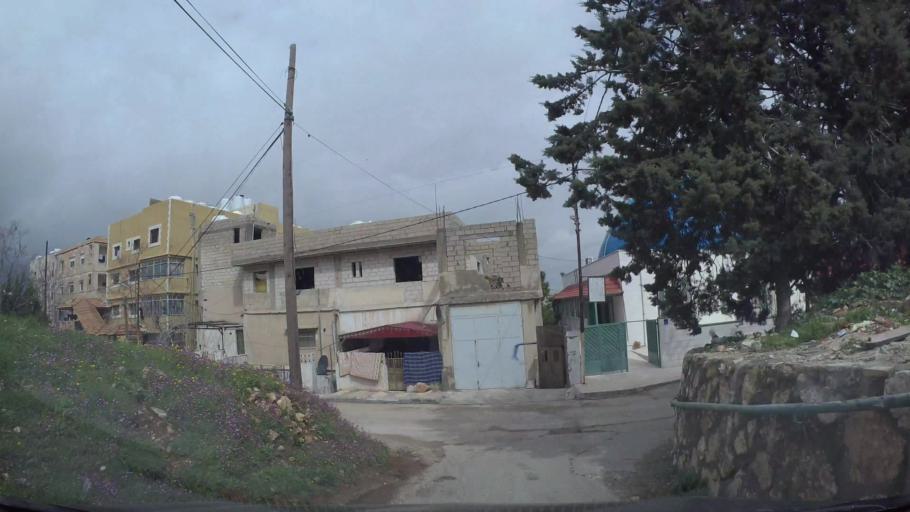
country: JO
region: Amman
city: Wadi as Sir
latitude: 31.9541
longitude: 35.8315
